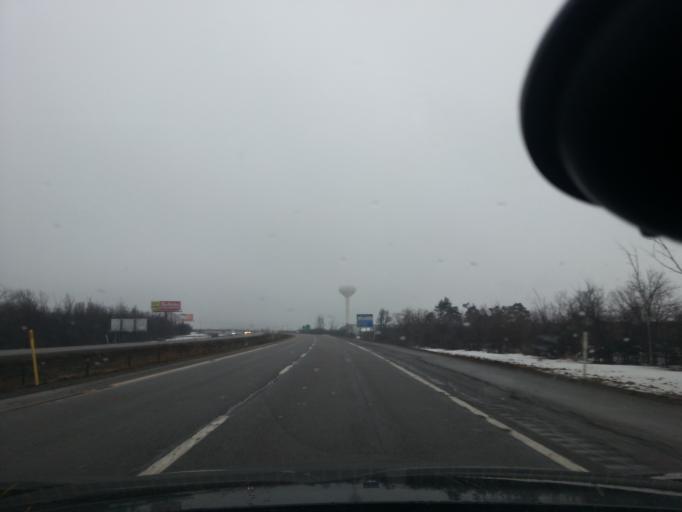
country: US
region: New York
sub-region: Jefferson County
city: Watertown
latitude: 43.9941
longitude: -75.9373
